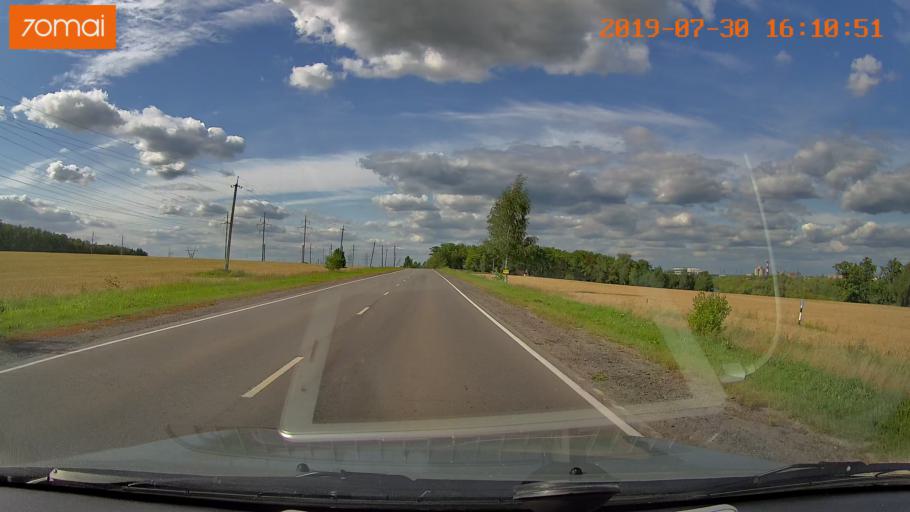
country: RU
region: Moskovskaya
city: Peski
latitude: 55.2676
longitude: 38.7145
